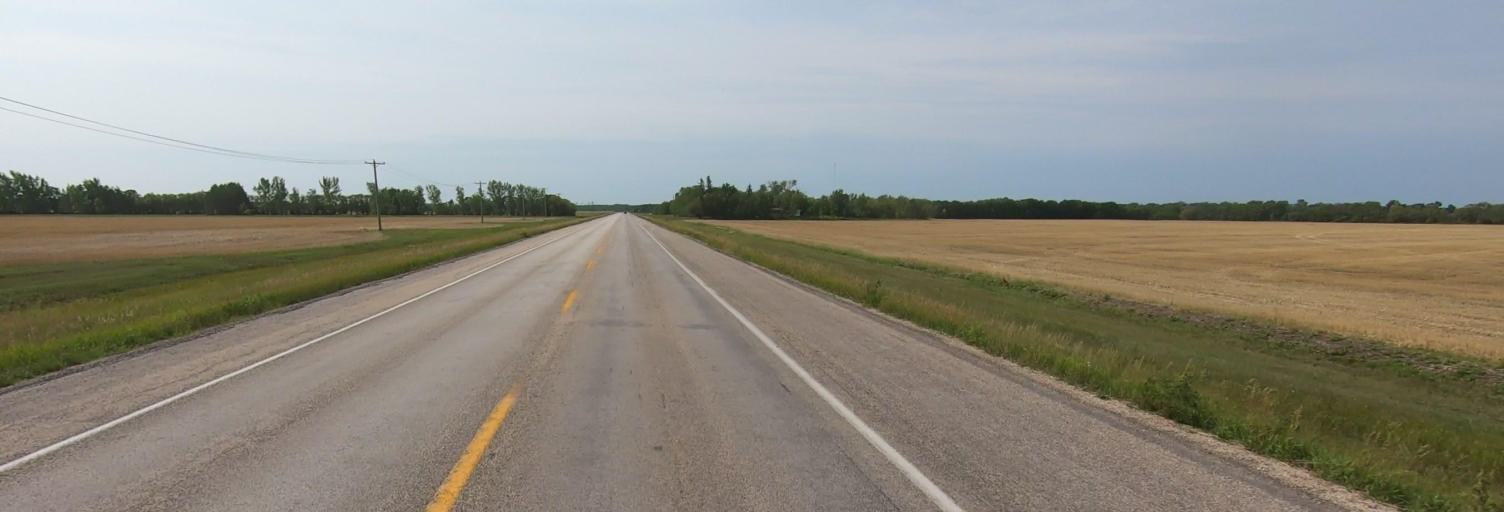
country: CA
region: Manitoba
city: Niverville
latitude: 49.6129
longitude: -97.1240
